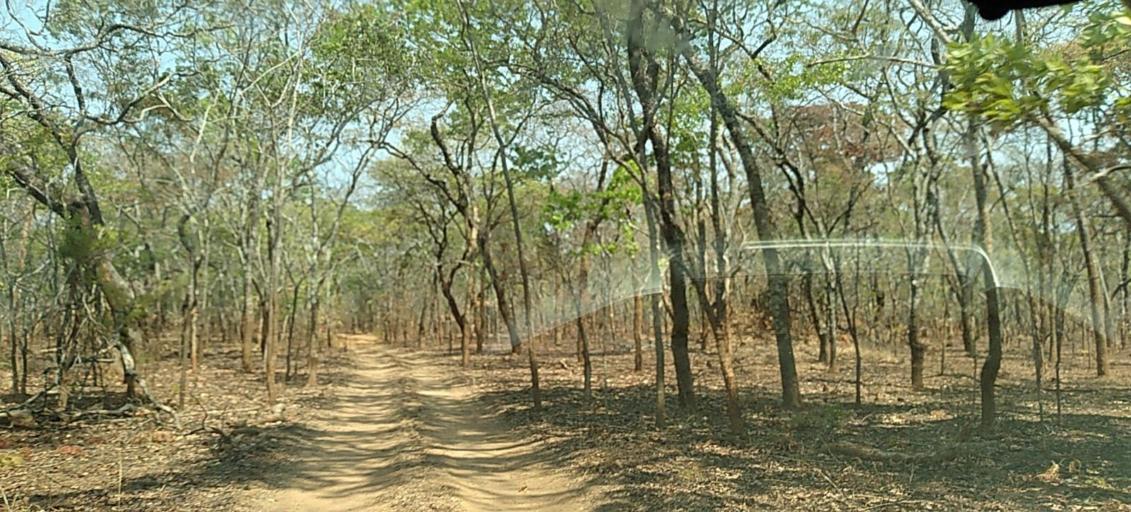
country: ZM
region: North-Western
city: Kasempa
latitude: -13.3936
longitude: 25.5941
